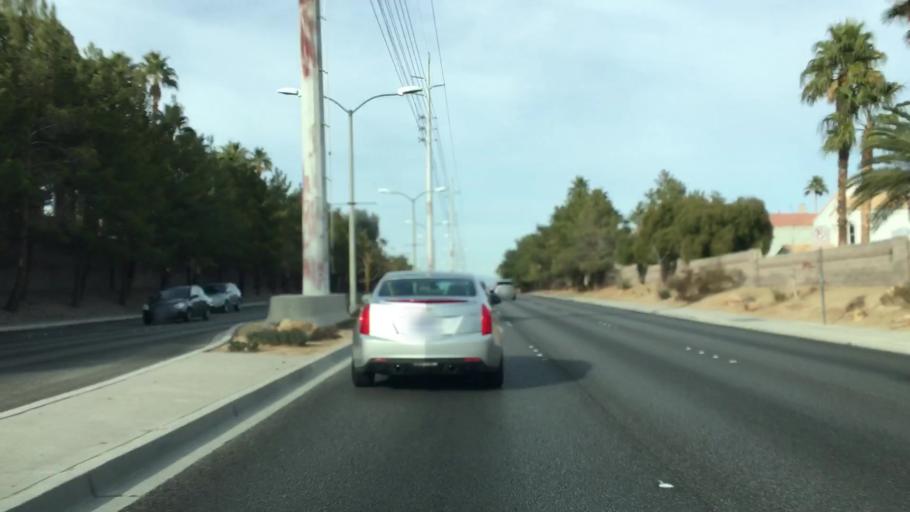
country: US
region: Nevada
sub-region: Clark County
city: Whitney
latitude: 36.0460
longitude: -115.0823
